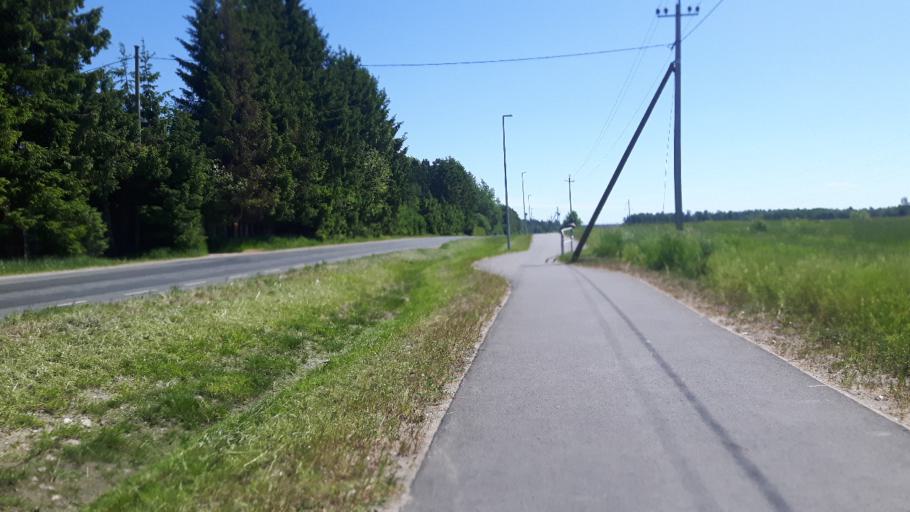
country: EE
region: Harju
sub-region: Saku vald
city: Saku
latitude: 59.2149
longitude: 24.6783
